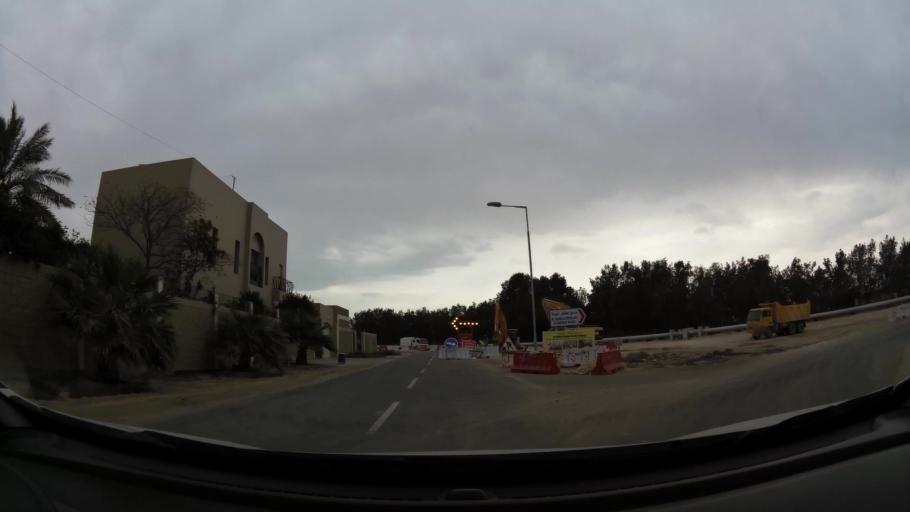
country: BH
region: Central Governorate
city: Madinat Hamad
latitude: 26.1443
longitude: 50.4738
